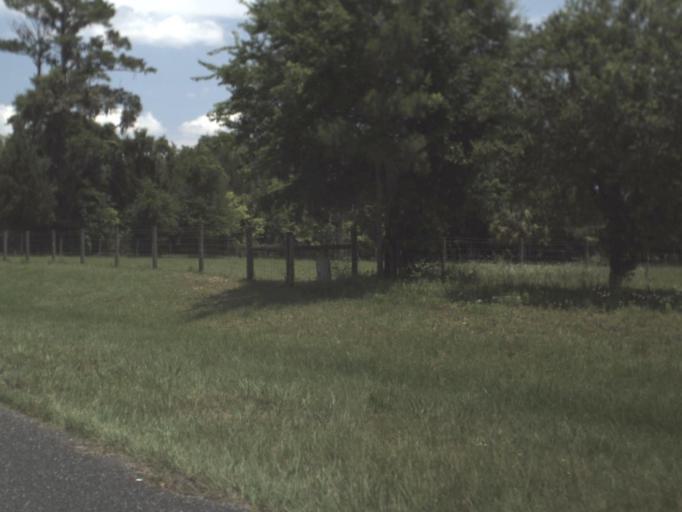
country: US
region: Florida
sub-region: Alachua County
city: Newberry
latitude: 29.6545
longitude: -82.5515
